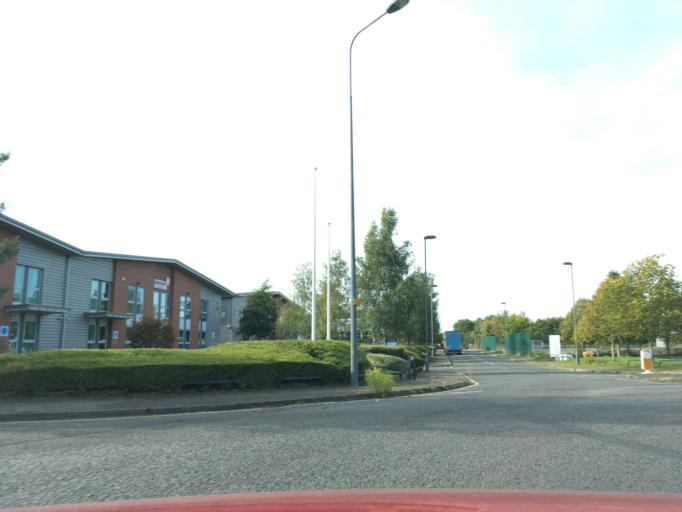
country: GB
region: England
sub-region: South Gloucestershire
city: Yate
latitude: 51.5375
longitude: -2.4406
